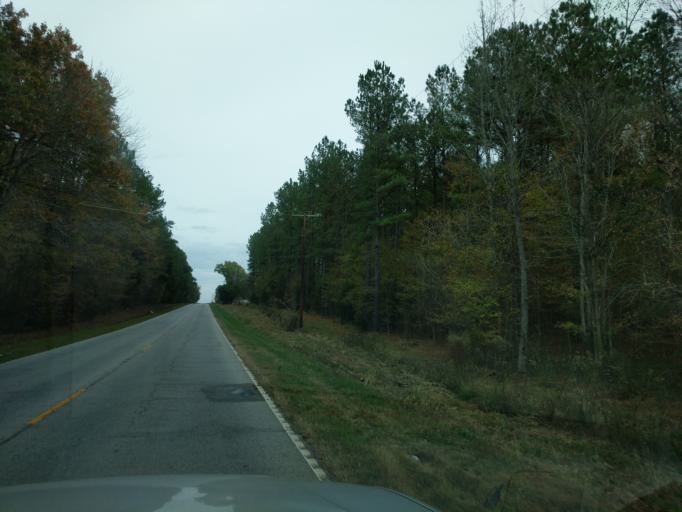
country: US
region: South Carolina
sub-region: Saluda County
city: Saluda
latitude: 34.0929
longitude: -81.7545
